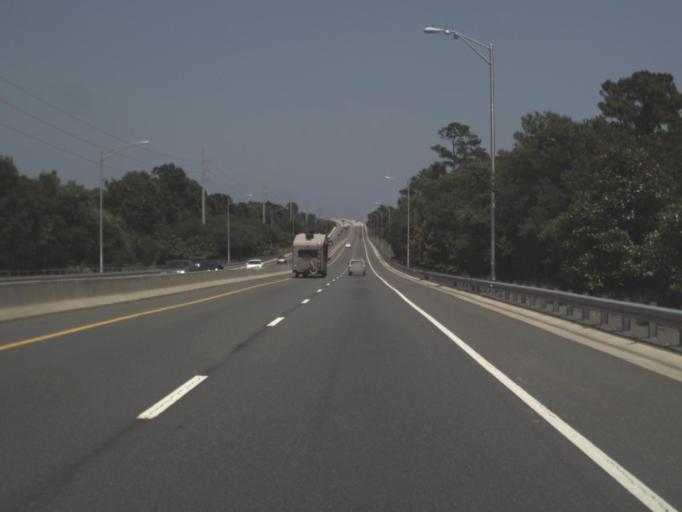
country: US
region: Florida
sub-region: Duval County
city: Atlantic Beach
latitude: 30.3586
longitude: -81.4566
